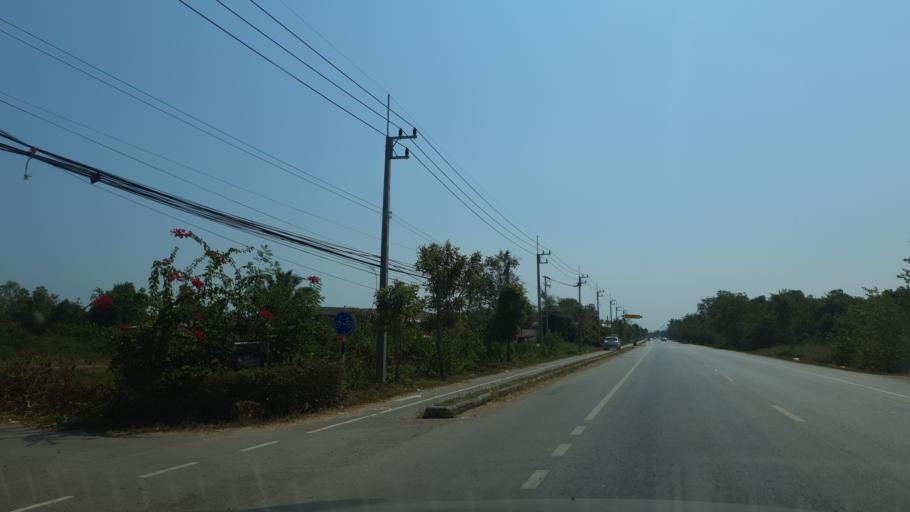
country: TH
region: Prachuap Khiri Khan
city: Pran Buri
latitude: 12.3536
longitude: 99.9387
